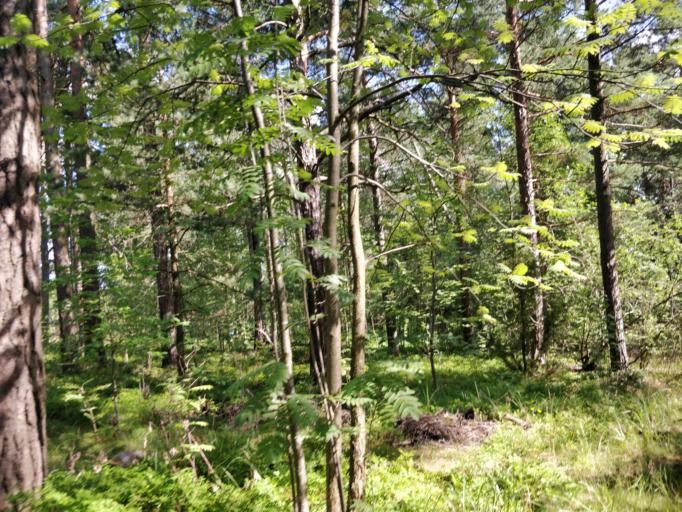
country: FI
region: Uusimaa
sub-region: Helsinki
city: Helsinki
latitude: 60.1802
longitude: 24.9932
